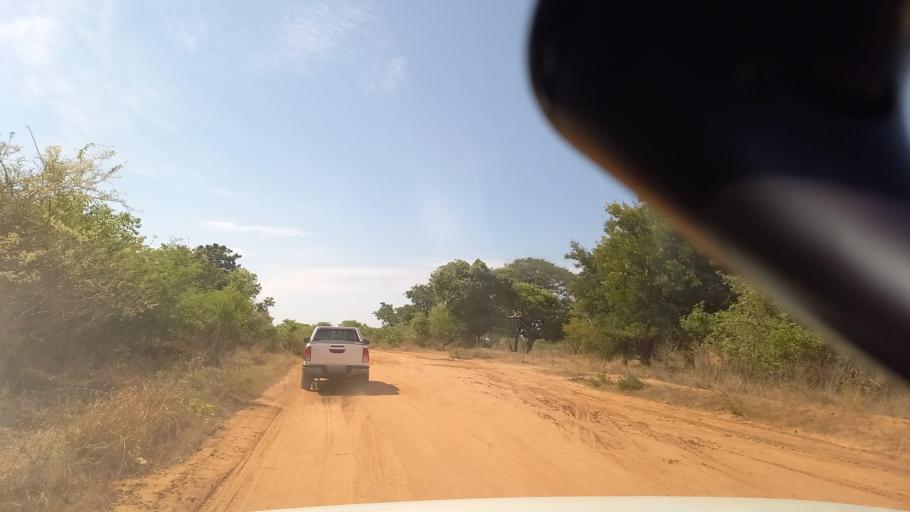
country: ZM
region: Southern
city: Mazabuka
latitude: -16.0375
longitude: 27.6178
